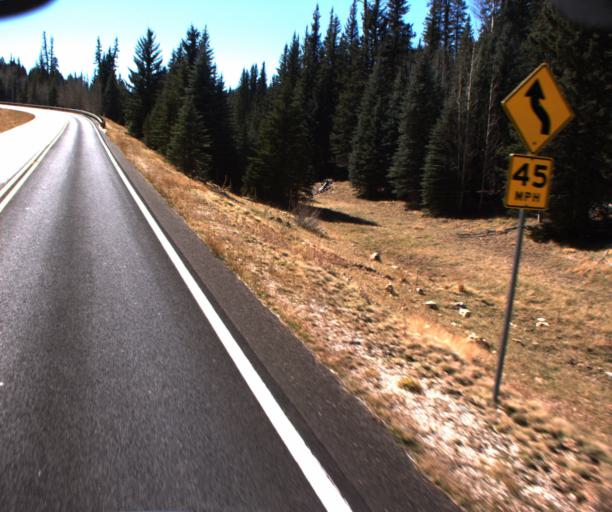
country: US
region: Arizona
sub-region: Coconino County
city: Grand Canyon
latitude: 36.5379
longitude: -112.1580
